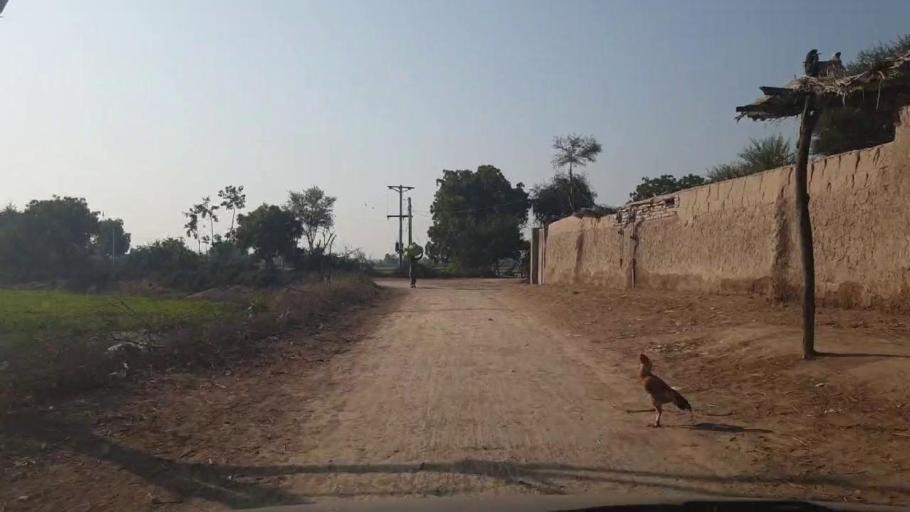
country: PK
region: Sindh
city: Tando Adam
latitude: 25.7490
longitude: 68.6045
